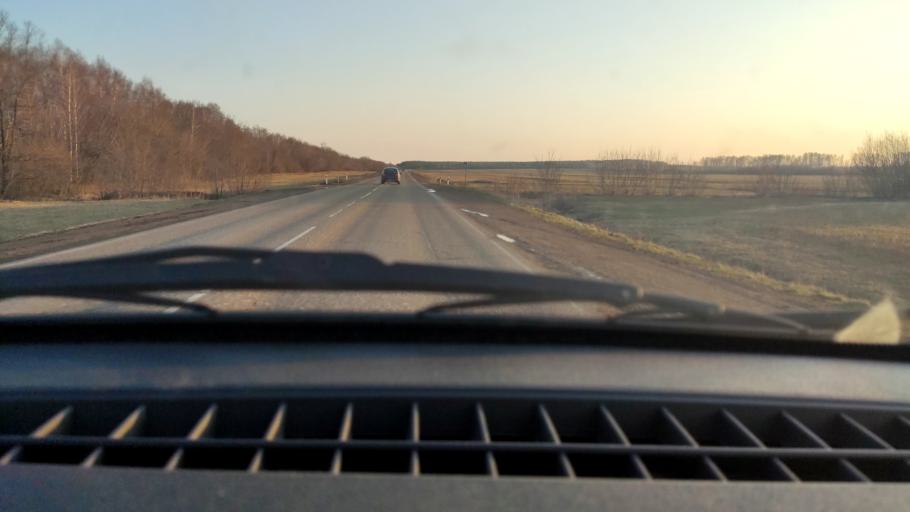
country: RU
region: Bashkortostan
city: Davlekanovo
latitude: 54.2594
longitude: 55.0887
